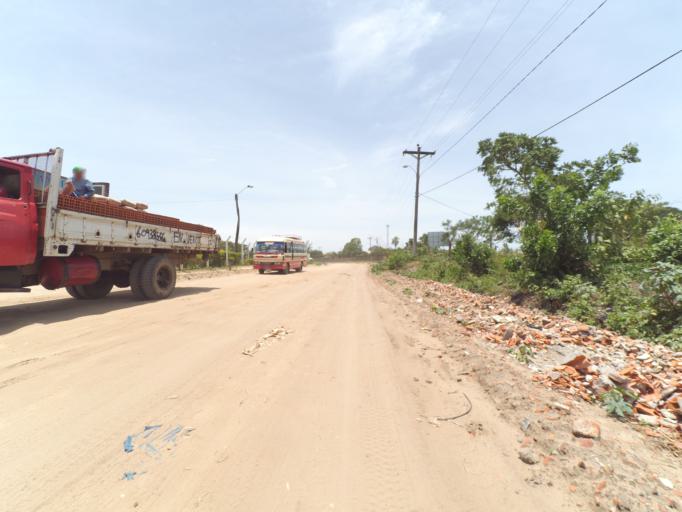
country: BO
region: Santa Cruz
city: Santa Cruz de la Sierra
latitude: -17.8234
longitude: -63.2469
